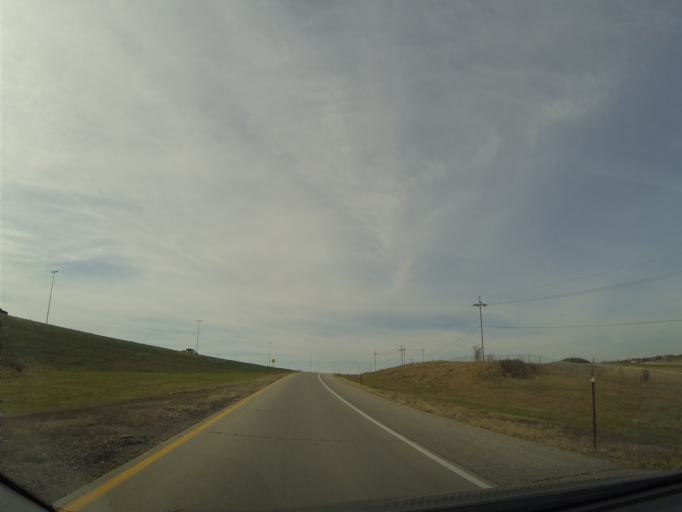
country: US
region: Nebraska
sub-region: Douglas County
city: Elkhorn
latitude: 41.2636
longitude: -96.2169
